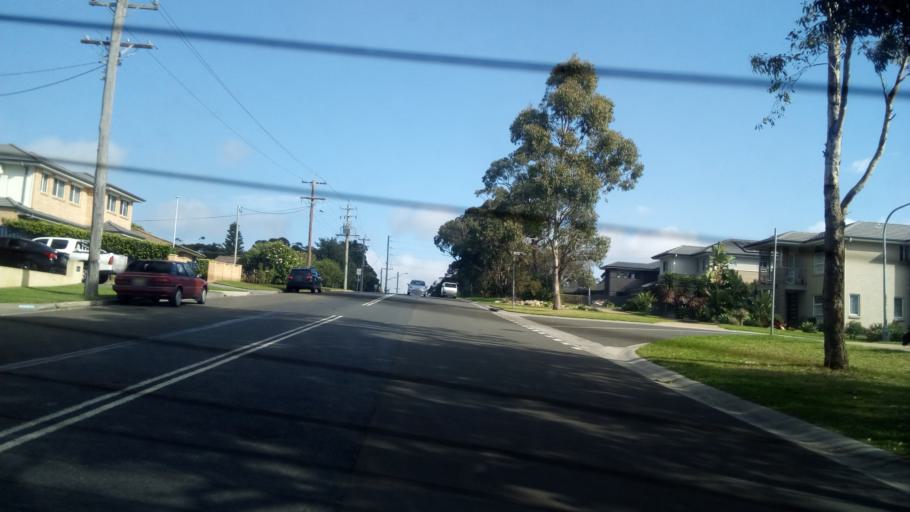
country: AU
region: New South Wales
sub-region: Wollongong
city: Helensburgh
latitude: -34.1997
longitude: 150.9804
